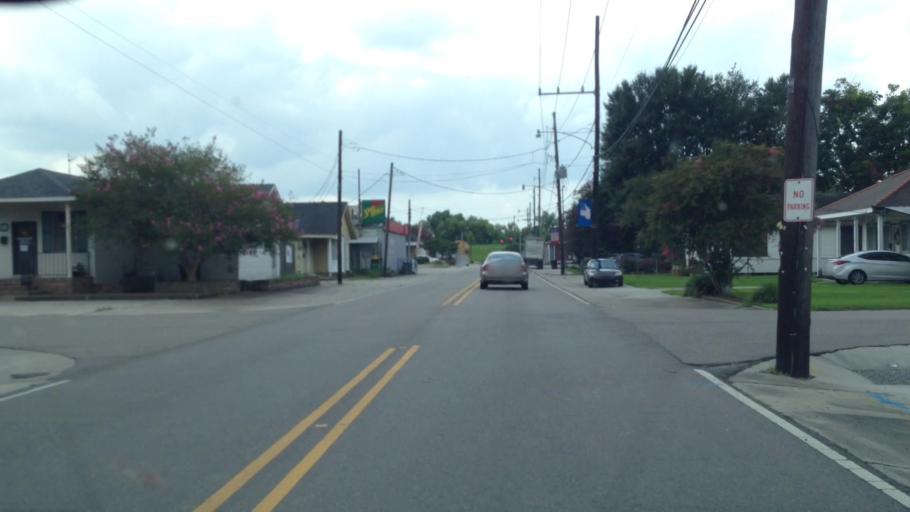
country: US
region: Louisiana
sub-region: Saint Charles Parish
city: Norco
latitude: 29.9991
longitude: -90.4127
